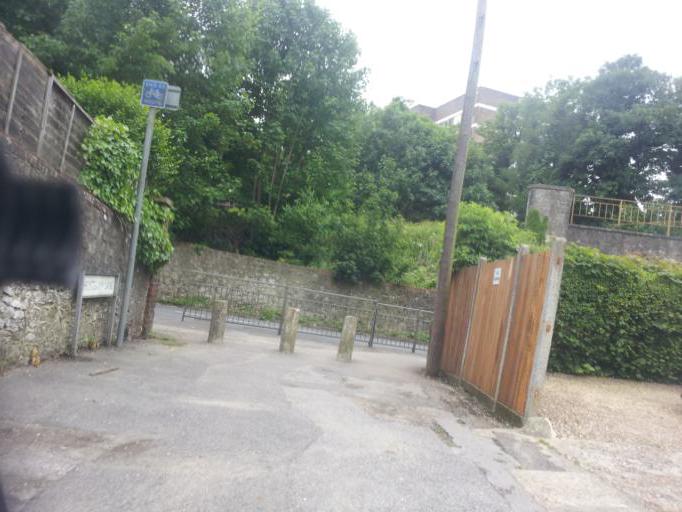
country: GB
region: England
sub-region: Kent
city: Maidstone
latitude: 51.2739
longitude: 0.5349
